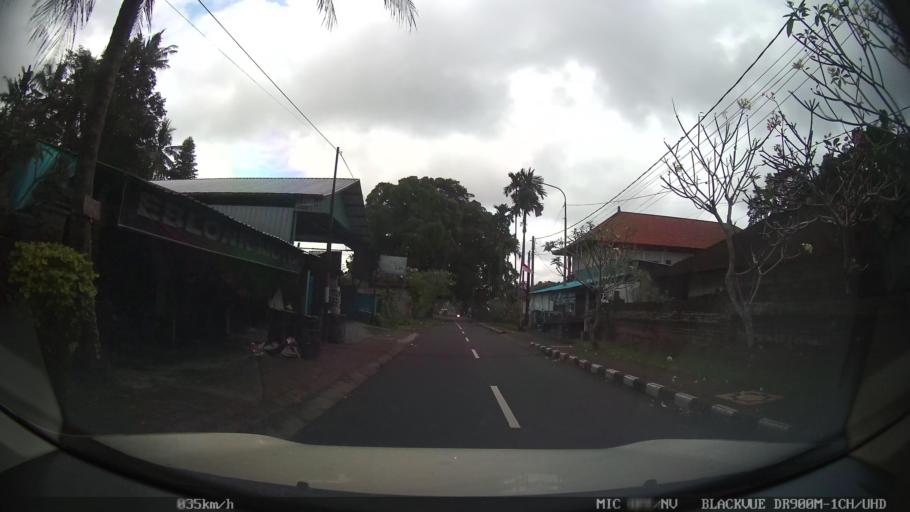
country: ID
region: Bali
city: Banjar Sempidi
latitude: -8.5230
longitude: 115.2032
